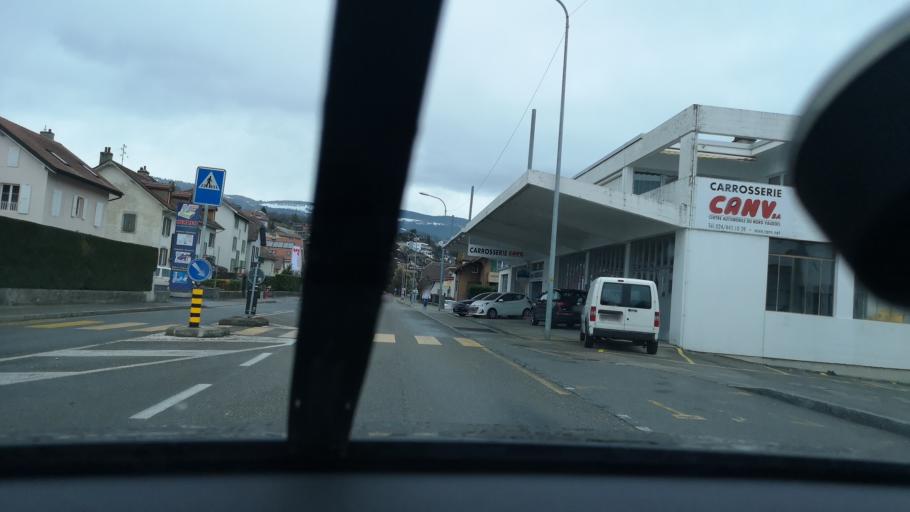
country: CH
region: Vaud
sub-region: Jura-Nord vaudois District
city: Montagny
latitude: 46.7965
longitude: 6.6284
